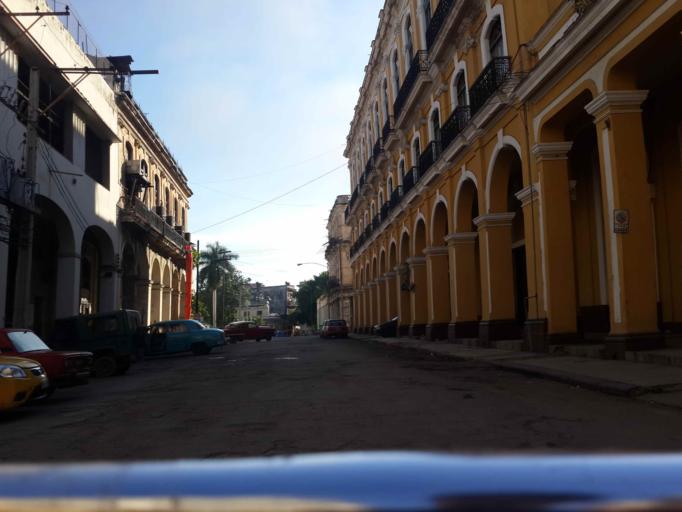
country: CU
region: La Habana
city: La Habana Vieja
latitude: 23.1308
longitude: -82.3564
